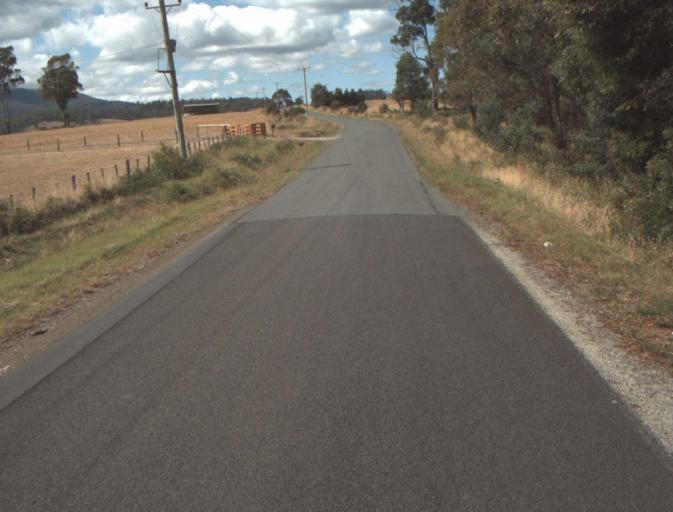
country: AU
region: Tasmania
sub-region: Launceston
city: Mayfield
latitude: -41.2301
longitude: 147.1450
